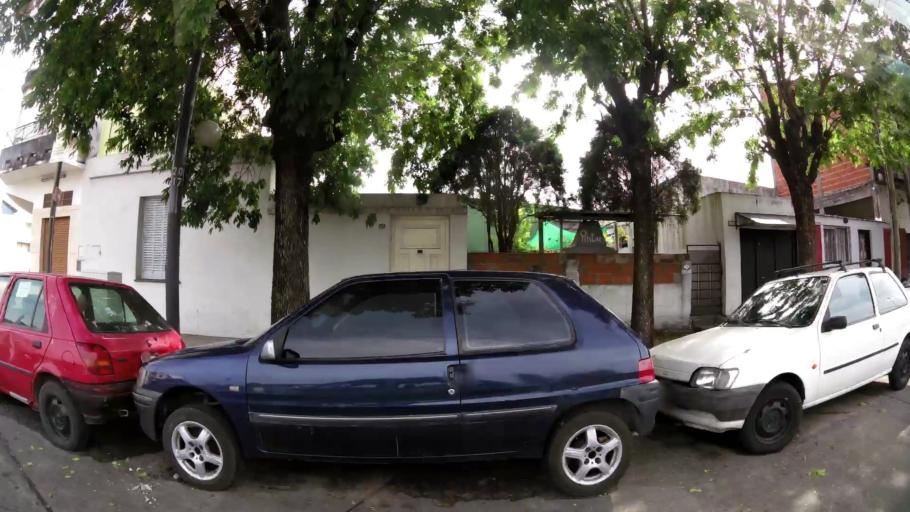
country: AR
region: Buenos Aires F.D.
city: Villa Lugano
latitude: -34.6541
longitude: -58.4811
